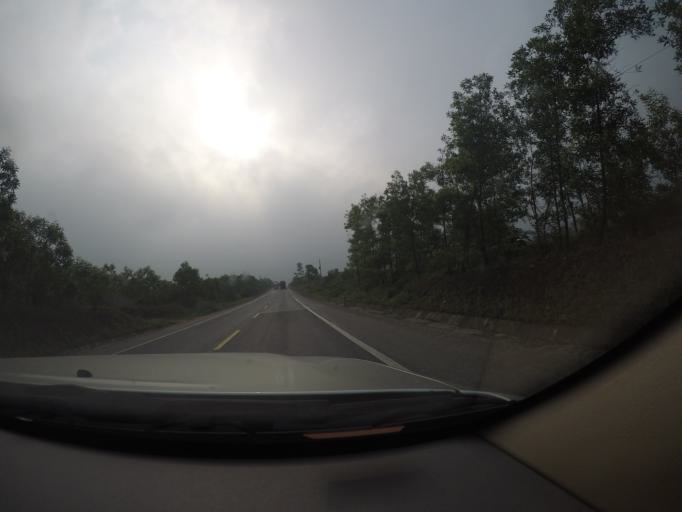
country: VN
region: Ha Tinh
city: Ky Anh
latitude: 18.0395
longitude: 106.2959
